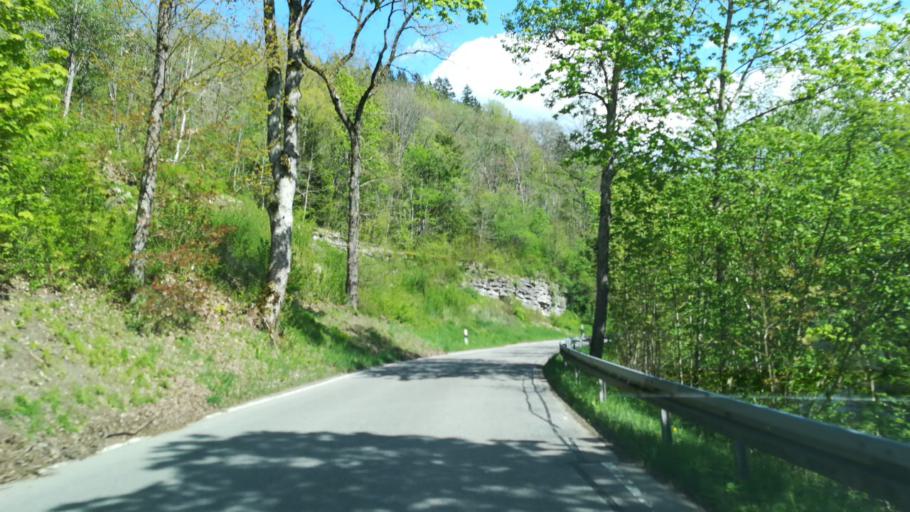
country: DE
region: Baden-Wuerttemberg
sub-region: Freiburg Region
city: Blumberg
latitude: 47.8430
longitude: 8.4756
